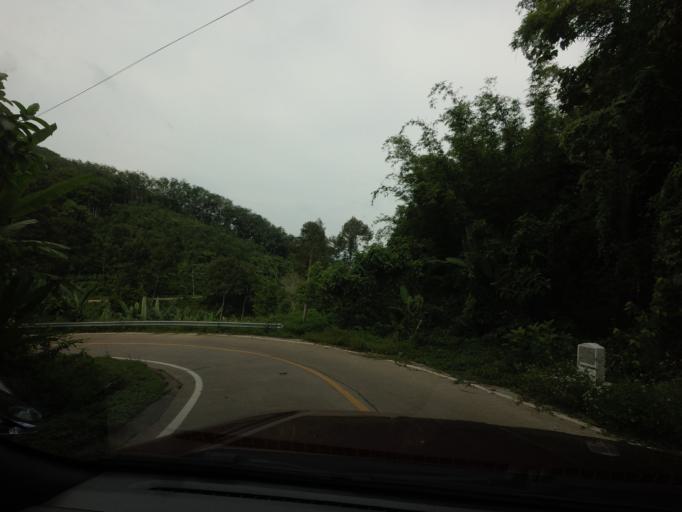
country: TH
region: Yala
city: Than To
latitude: 6.0665
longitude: 101.3570
